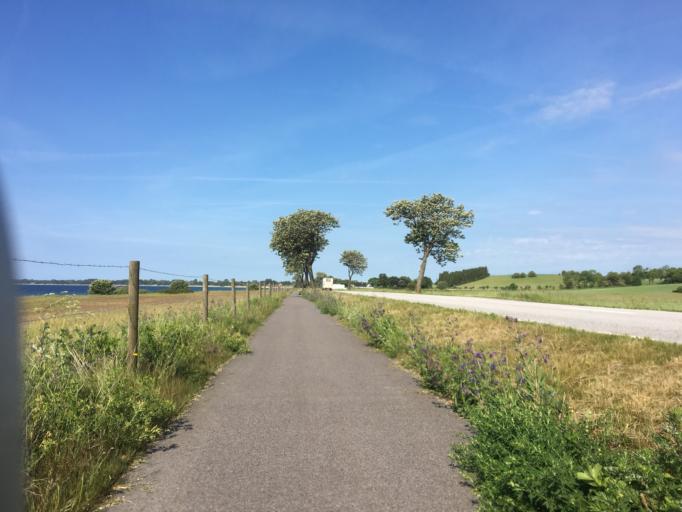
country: SE
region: Skane
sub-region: Skurups Kommun
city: Rydsgard
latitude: 55.4180
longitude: 13.6621
